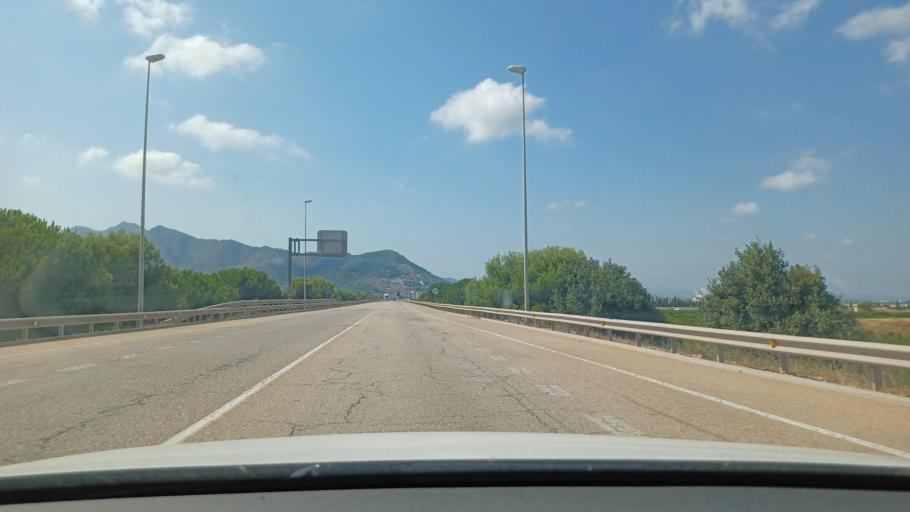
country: ES
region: Valencia
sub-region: Provincia de Castello
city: Villavieja
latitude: 39.8380
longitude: -0.1694
